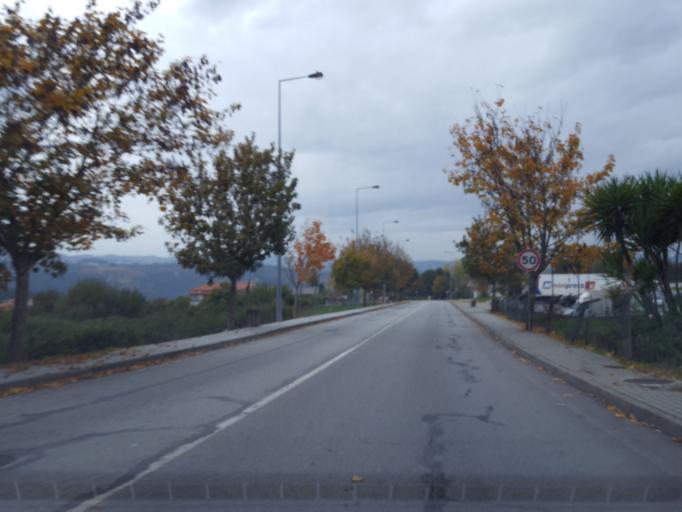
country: PT
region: Porto
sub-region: Marco de Canaveses
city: Marco de Canavezes
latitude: 41.1783
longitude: -8.1549
